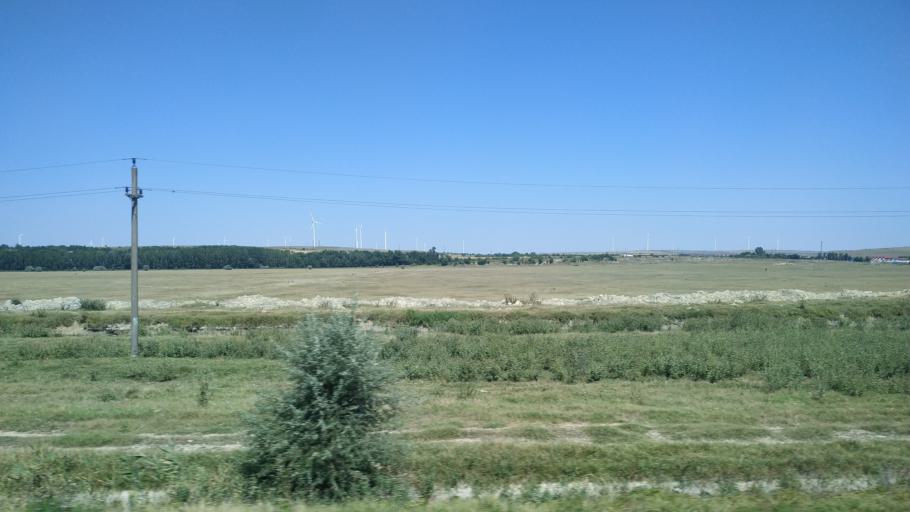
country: RO
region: Constanta
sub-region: Comuna Mircea Voda
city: Mircea Voda
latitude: 44.2643
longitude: 28.1643
